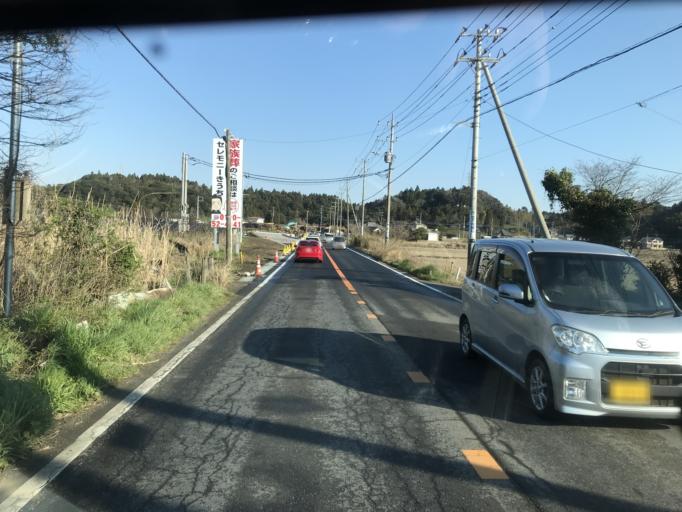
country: JP
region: Chiba
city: Sawara
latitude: 35.8737
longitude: 140.4956
